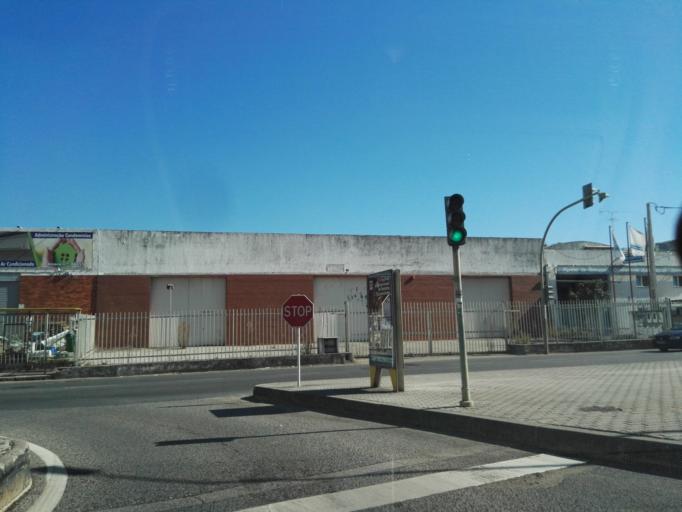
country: PT
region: Lisbon
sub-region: Odivelas
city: Povoa de Santo Adriao
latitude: 38.8065
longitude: -9.1577
